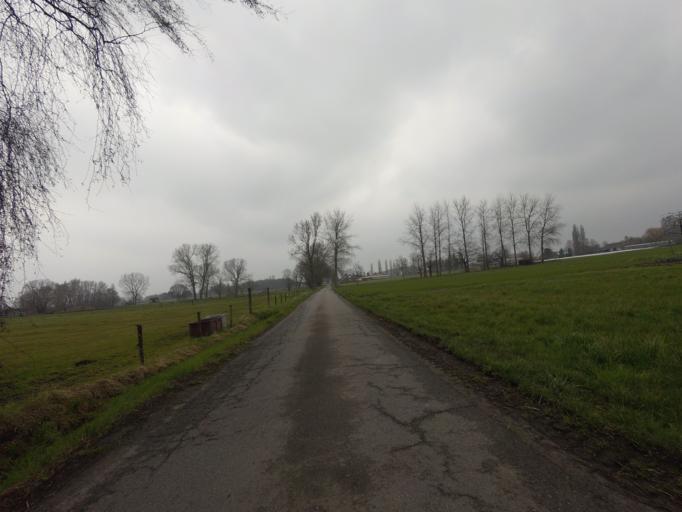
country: BE
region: Flanders
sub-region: Provincie Antwerpen
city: Putte
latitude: 51.0655
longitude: 4.5946
